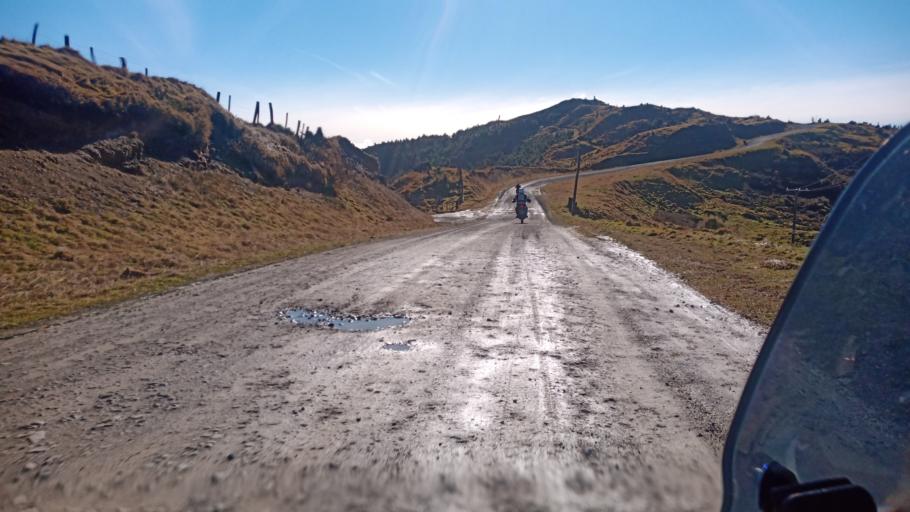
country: NZ
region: Gisborne
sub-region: Gisborne District
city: Gisborne
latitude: -38.1818
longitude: 177.8228
